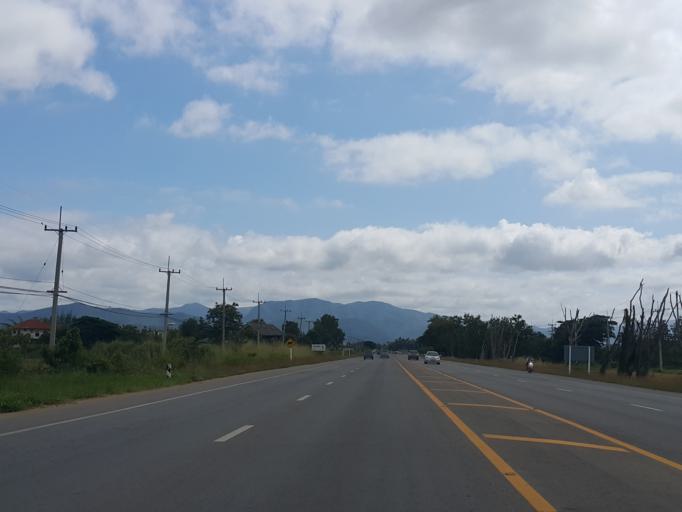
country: TH
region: Chiang Mai
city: San Kamphaeng
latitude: 18.7183
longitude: 99.1148
